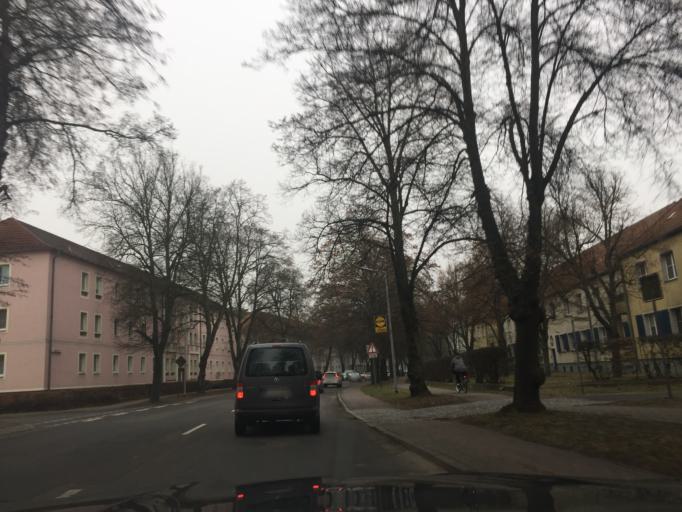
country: DE
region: Brandenburg
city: Hennigsdorf
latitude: 52.6479
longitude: 13.2001
